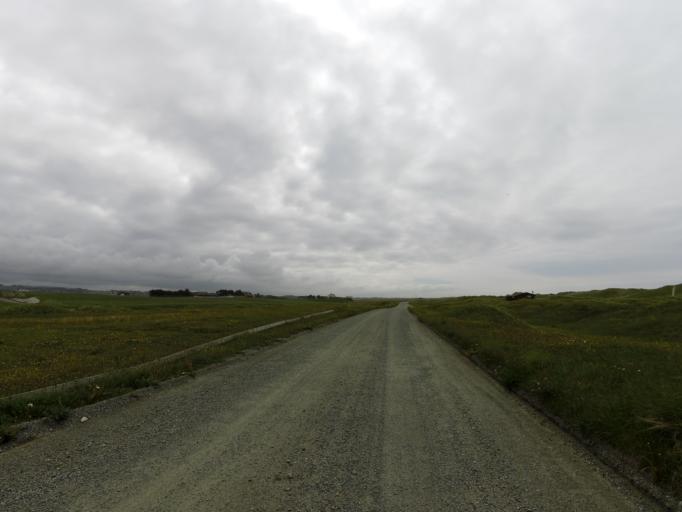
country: NO
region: Rogaland
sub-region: Klepp
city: Kleppe
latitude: 58.8076
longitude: 5.5511
